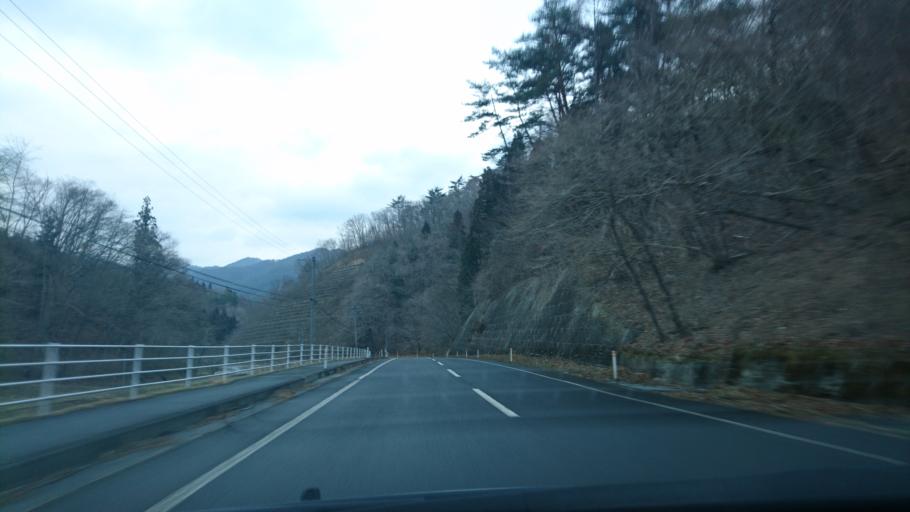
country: JP
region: Iwate
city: Ofunato
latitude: 39.0154
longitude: 141.5468
